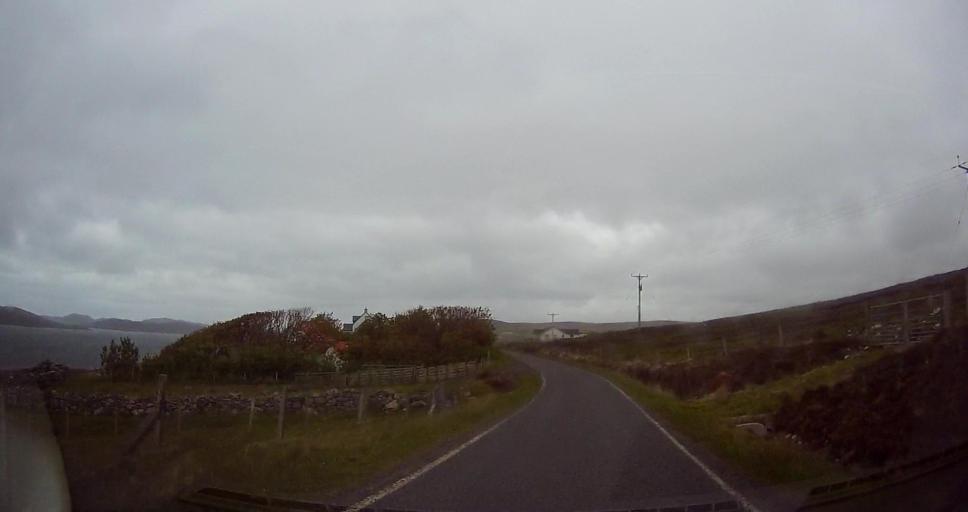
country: GB
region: Scotland
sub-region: Shetland Islands
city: Lerwick
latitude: 60.2935
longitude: -1.3646
